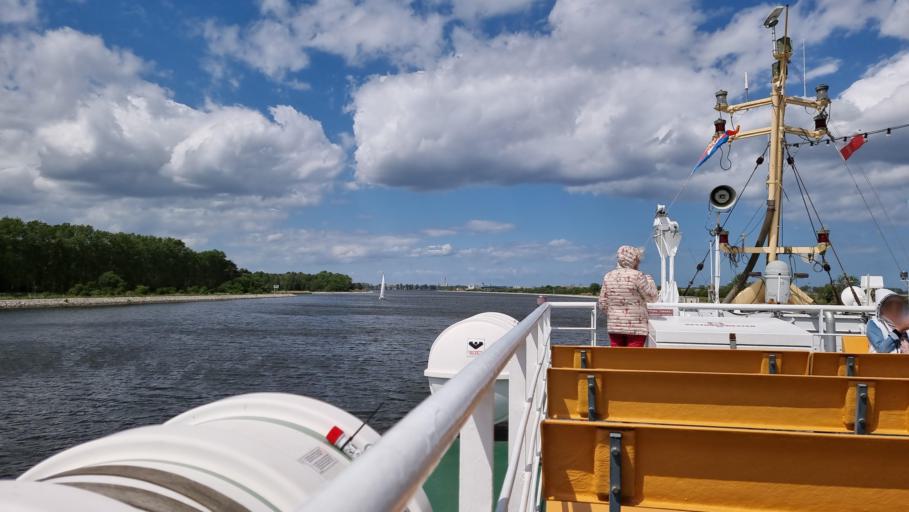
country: PL
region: West Pomeranian Voivodeship
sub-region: Swinoujscie
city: Swinoujscie
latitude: 53.8754
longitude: 14.2741
